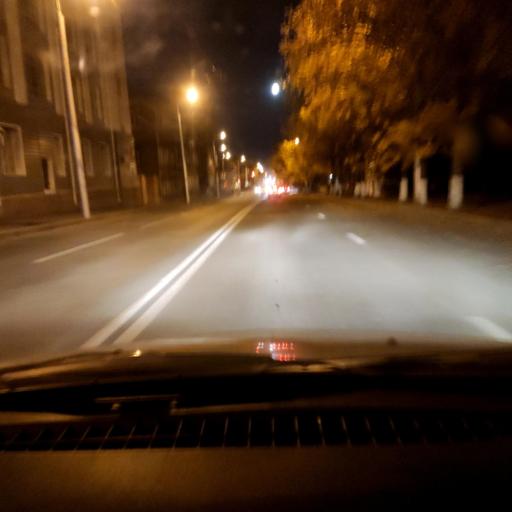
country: RU
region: Bashkortostan
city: Ufa
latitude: 54.7285
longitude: 55.9329
